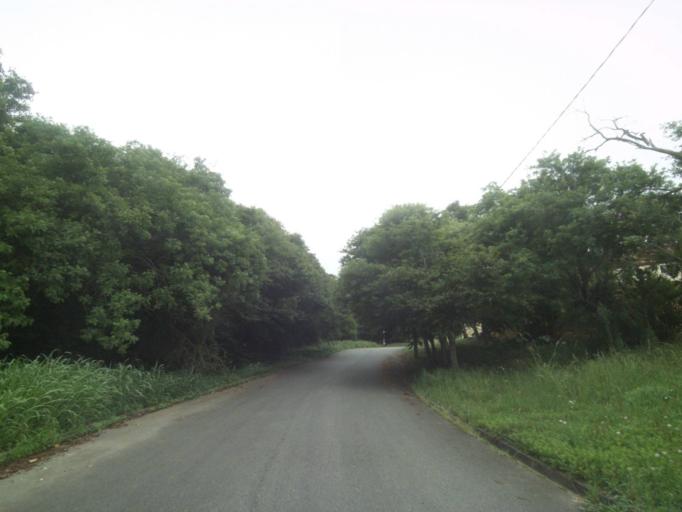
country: BR
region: Parana
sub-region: Curitiba
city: Curitiba
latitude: -25.4010
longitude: -49.2924
